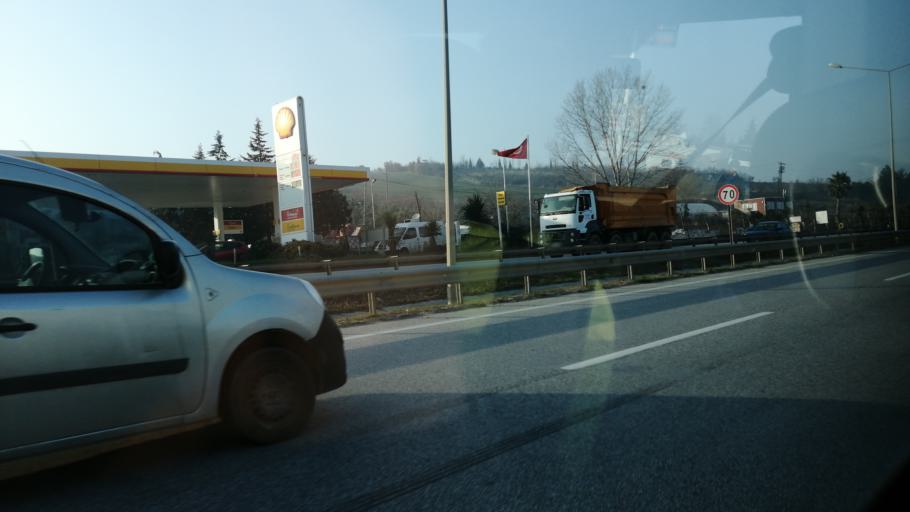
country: TR
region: Yalova
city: Yalova
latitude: 40.6235
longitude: 29.2709
